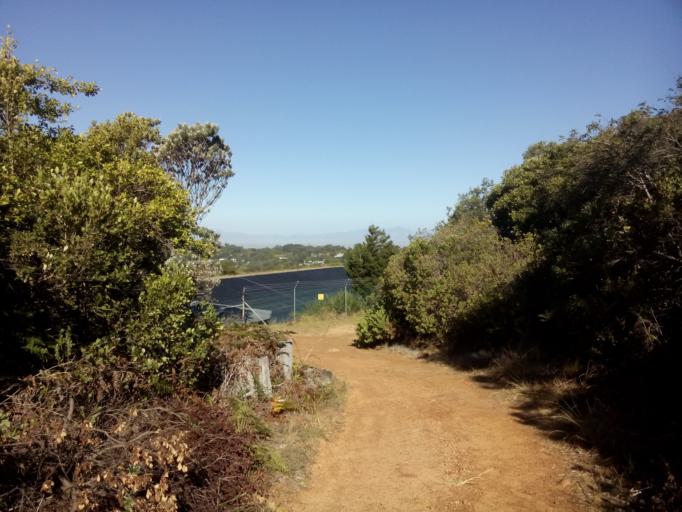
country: ZA
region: Western Cape
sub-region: City of Cape Town
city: Newlands
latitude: -33.9906
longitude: 18.4257
